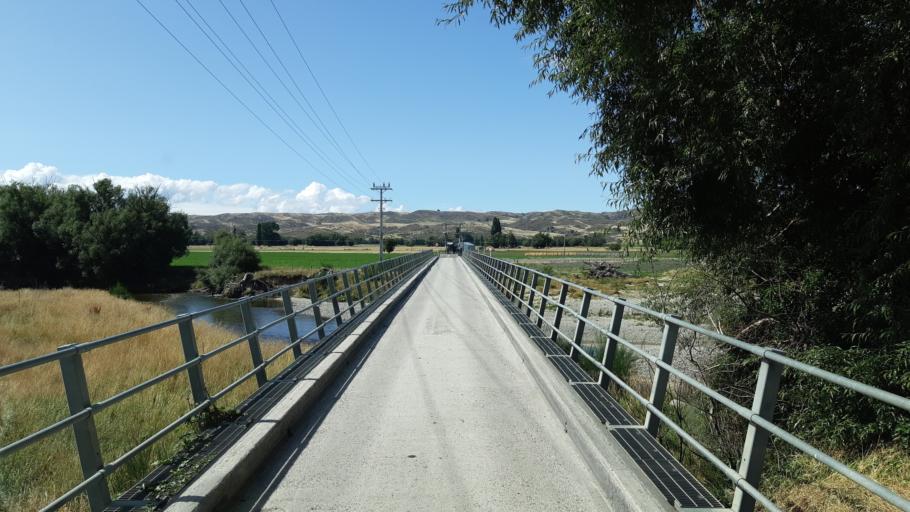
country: NZ
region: Otago
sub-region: Queenstown-Lakes District
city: Wanaka
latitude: -45.0950
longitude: 169.6020
